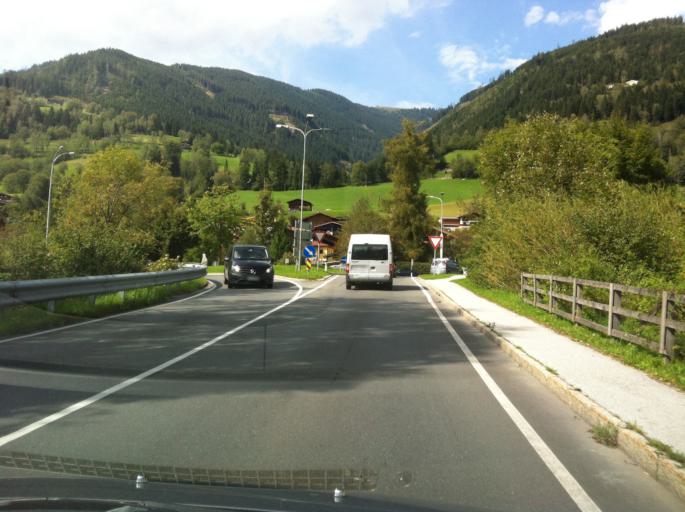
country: AT
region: Salzburg
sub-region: Politischer Bezirk Zell am See
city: Kaprun
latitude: 47.2900
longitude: 12.7454
